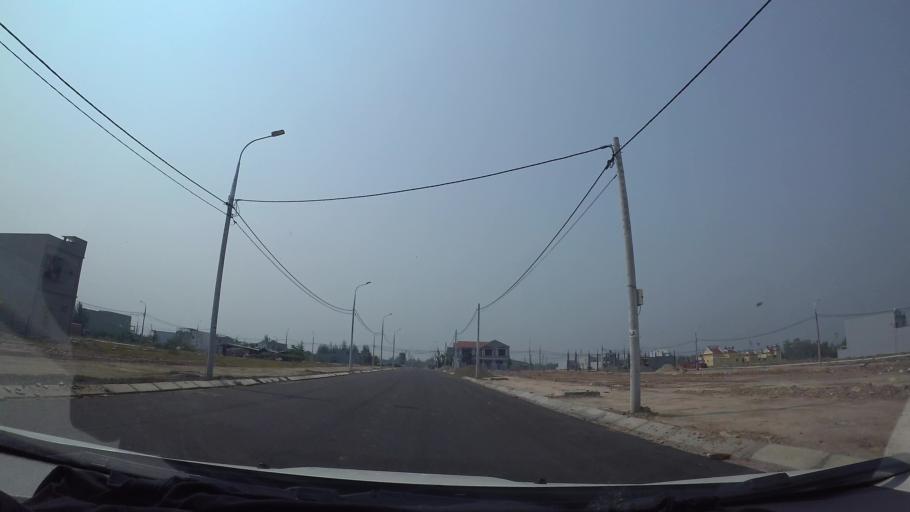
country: VN
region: Da Nang
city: Ngu Hanh Son
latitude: 15.9846
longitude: 108.2276
